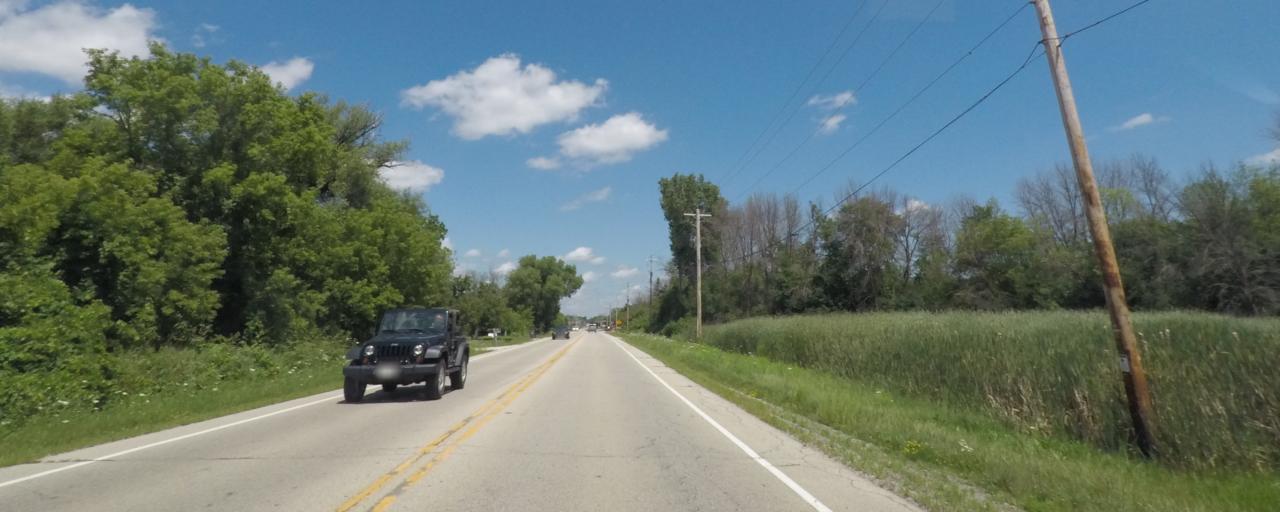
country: US
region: Wisconsin
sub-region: Waukesha County
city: Waukesha
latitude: 43.0453
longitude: -88.1859
